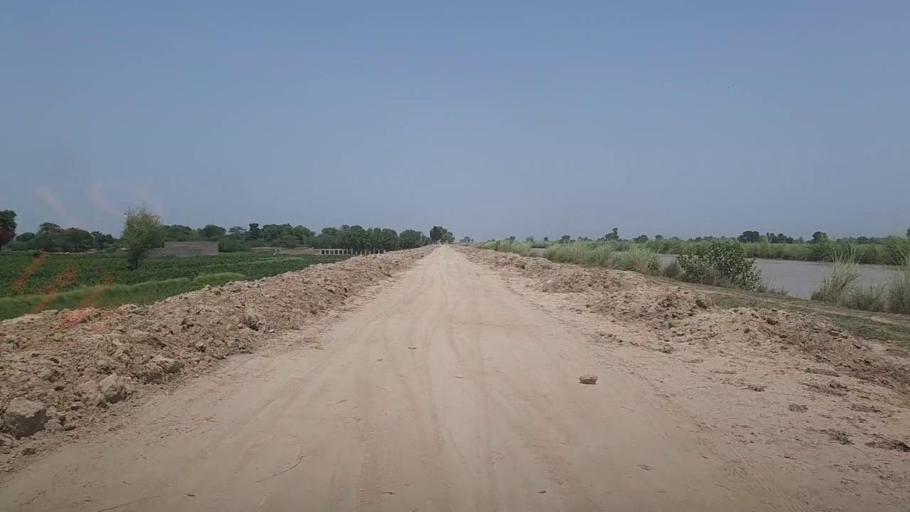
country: PK
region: Sindh
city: Pad Idan
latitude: 26.7885
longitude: 68.2767
